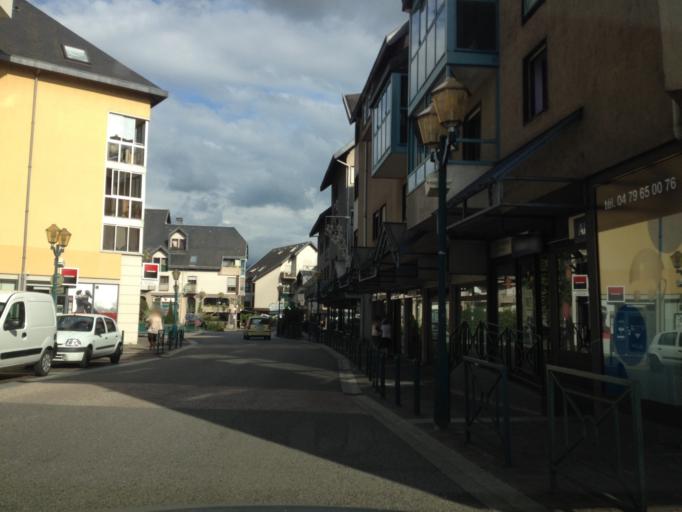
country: FR
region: Rhone-Alpes
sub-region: Departement de la Savoie
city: La Motte-Servolex
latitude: 45.5972
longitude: 5.8769
